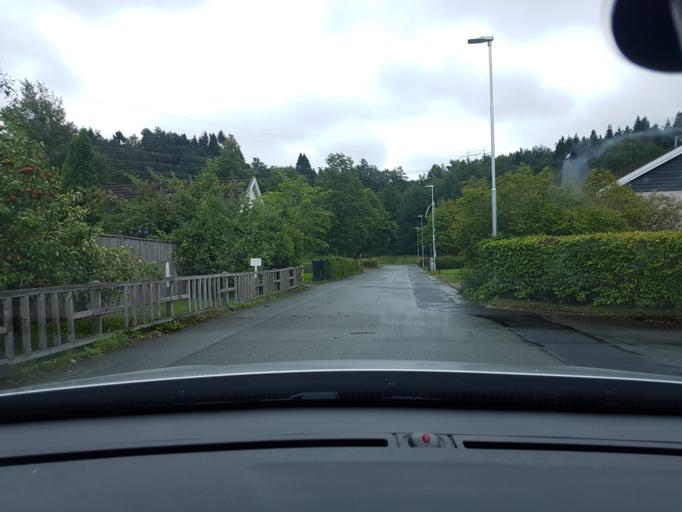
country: SE
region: Vaestra Goetaland
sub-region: Ale Kommun
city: Salanda
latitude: 57.9825
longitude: 12.2218
